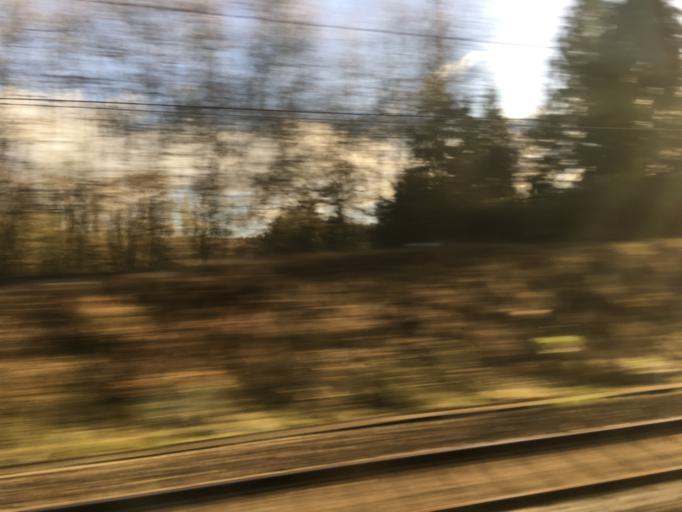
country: GB
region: England
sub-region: West Berkshire
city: Basildon
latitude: 51.4989
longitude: -1.1136
